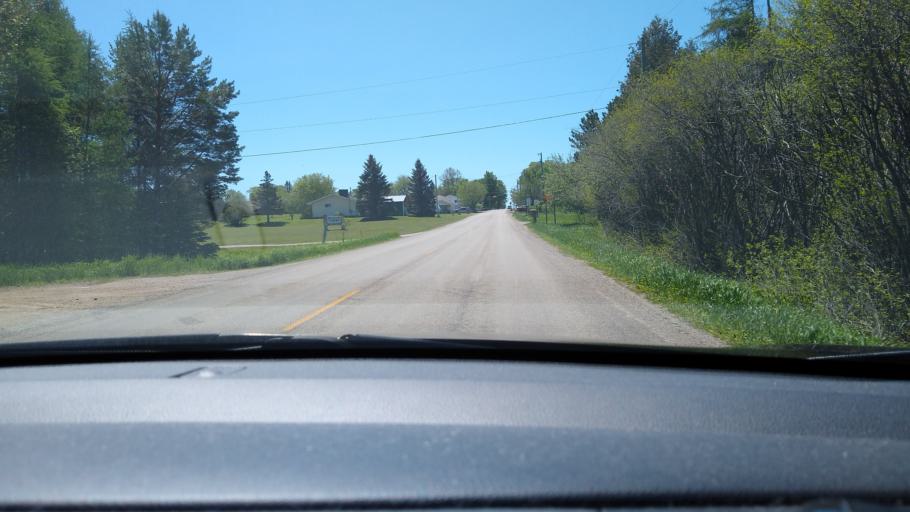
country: US
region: Michigan
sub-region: Delta County
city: Escanaba
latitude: 45.8285
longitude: -87.1832
